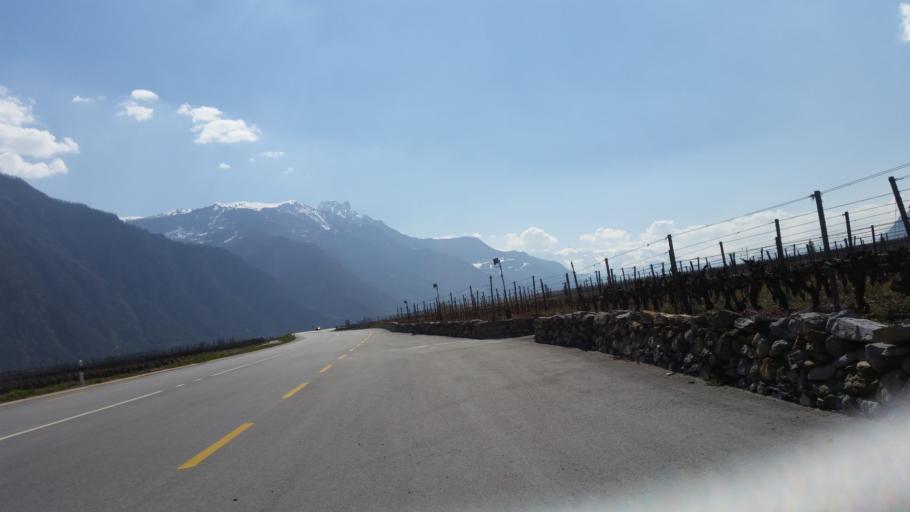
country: CH
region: Valais
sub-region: Conthey District
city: Ardon
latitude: 46.2029
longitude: 7.2488
